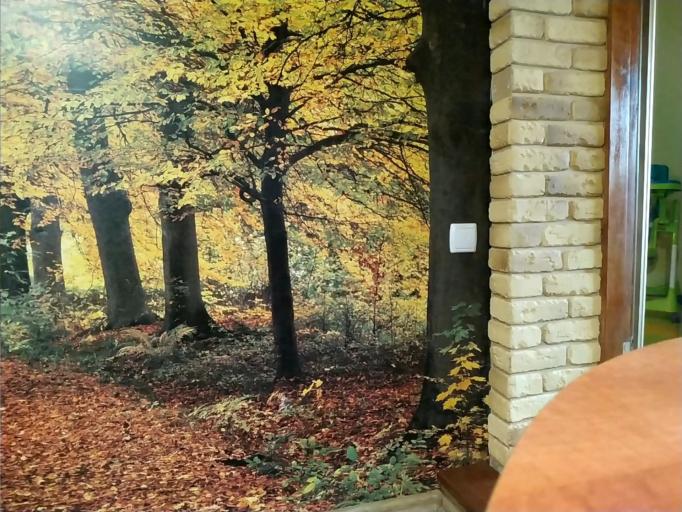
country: RU
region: Leningrad
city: Tolmachevo
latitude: 58.9281
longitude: 29.7281
